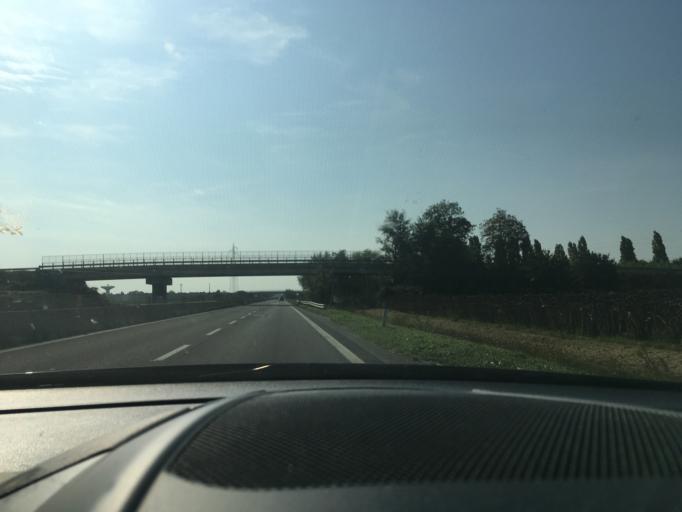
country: IT
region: Emilia-Romagna
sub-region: Provincia di Rimini
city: Bellaria-Igea Marina
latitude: 44.1372
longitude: 12.4614
